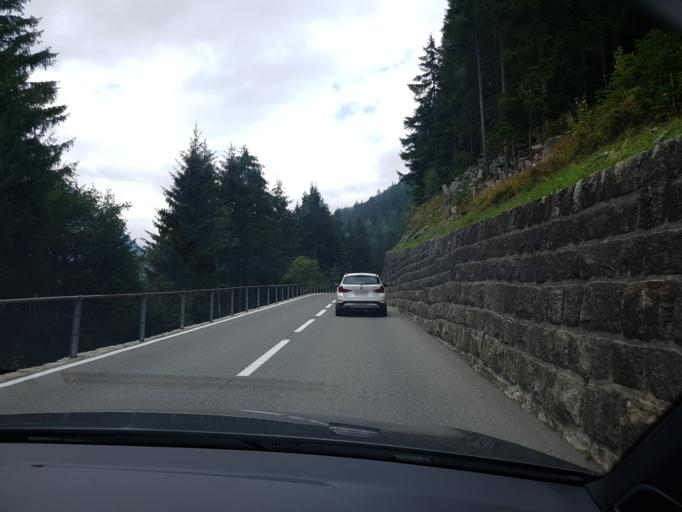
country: CH
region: Uri
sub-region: Uri
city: Andermatt
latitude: 46.7152
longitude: 8.5826
